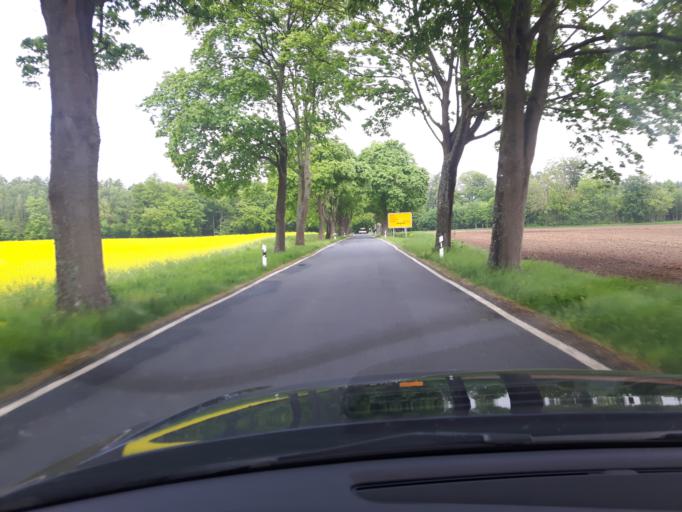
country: DE
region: Mecklenburg-Vorpommern
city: Velgast
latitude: 54.2269
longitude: 12.7325
